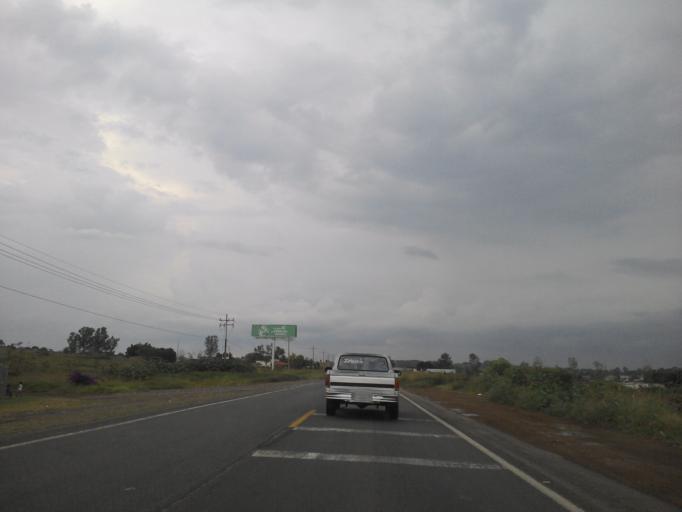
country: MX
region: Jalisco
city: Zapotlanejo
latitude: 20.6534
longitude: -103.0396
